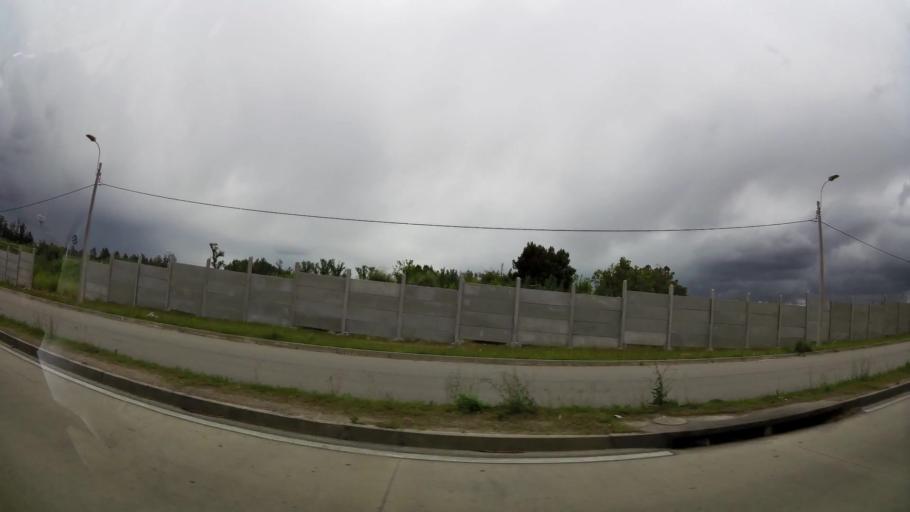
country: UY
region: Canelones
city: Toledo
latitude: -34.7964
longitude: -56.1460
